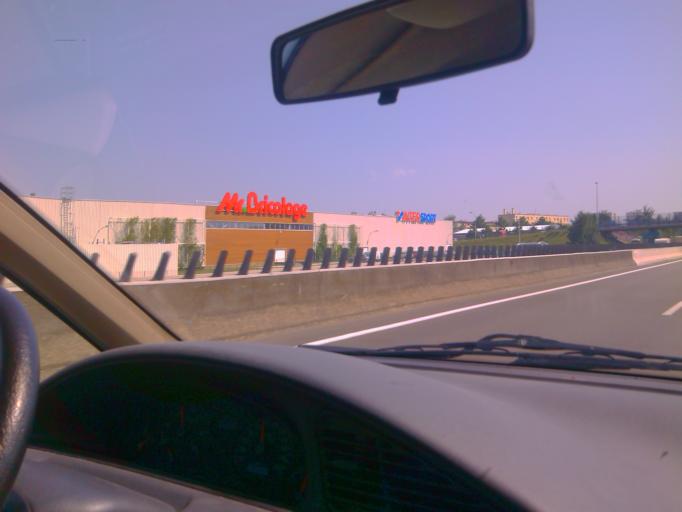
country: FR
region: Rhone-Alpes
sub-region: Departement du Rhone
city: Villefranche-sur-Saone
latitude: 45.9864
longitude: 4.7369
